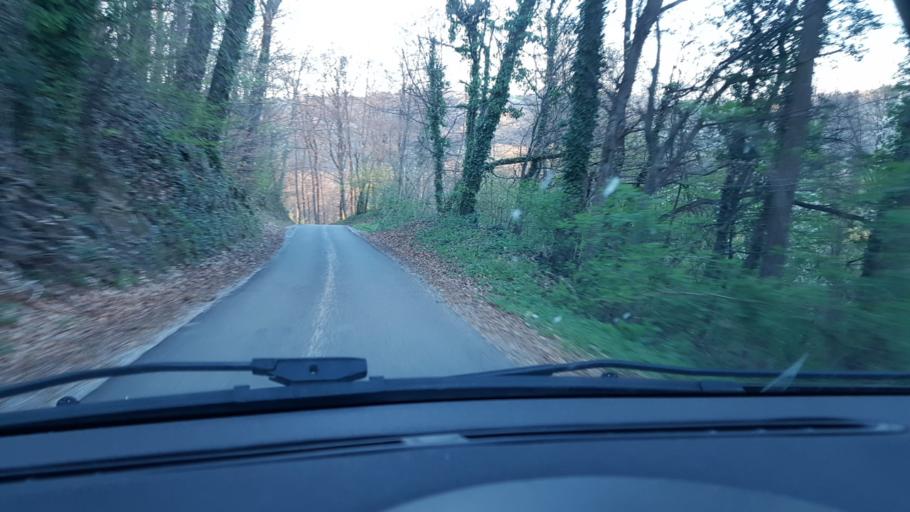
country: HR
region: Krapinsko-Zagorska
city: Pregrada
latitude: 46.1683
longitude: 15.6925
